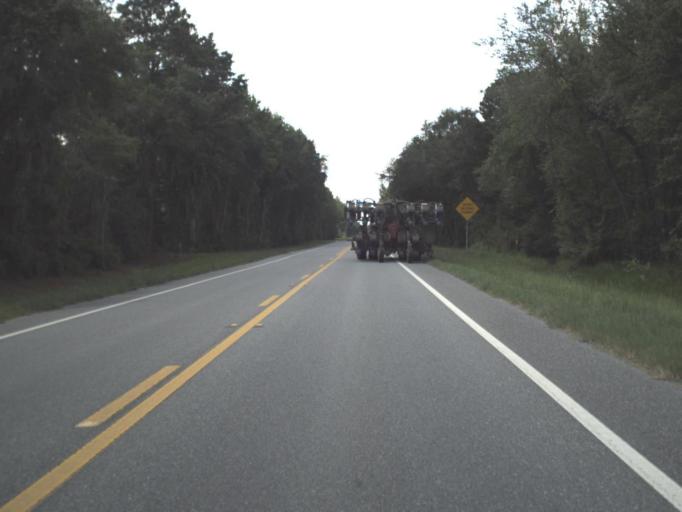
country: US
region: Florida
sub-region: Hamilton County
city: Jasper
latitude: 30.5652
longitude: -83.0737
